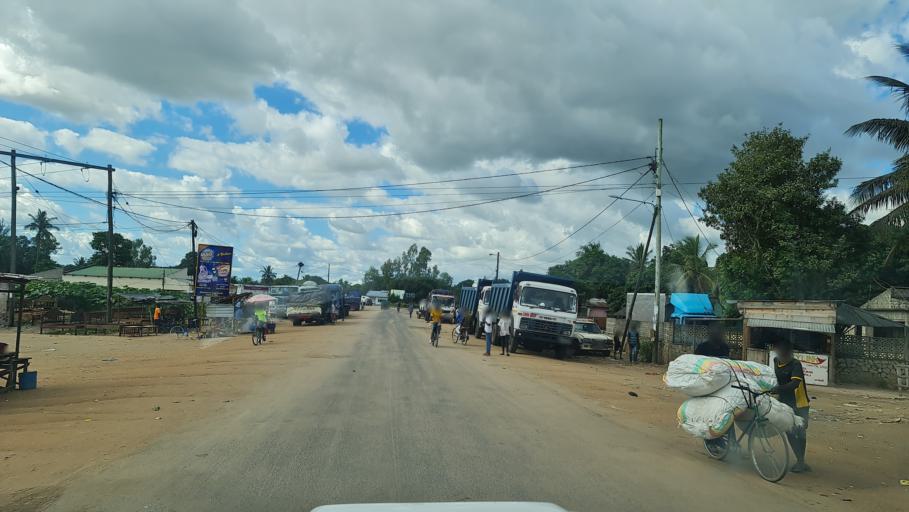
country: MZ
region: Zambezia
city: Quelimane
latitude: -17.5958
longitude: 36.8131
